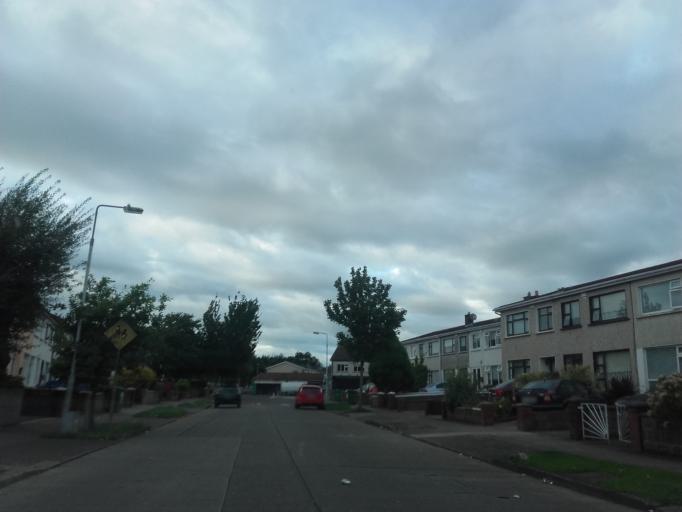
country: IE
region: Leinster
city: Tallaght
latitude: 53.2863
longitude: -6.3819
